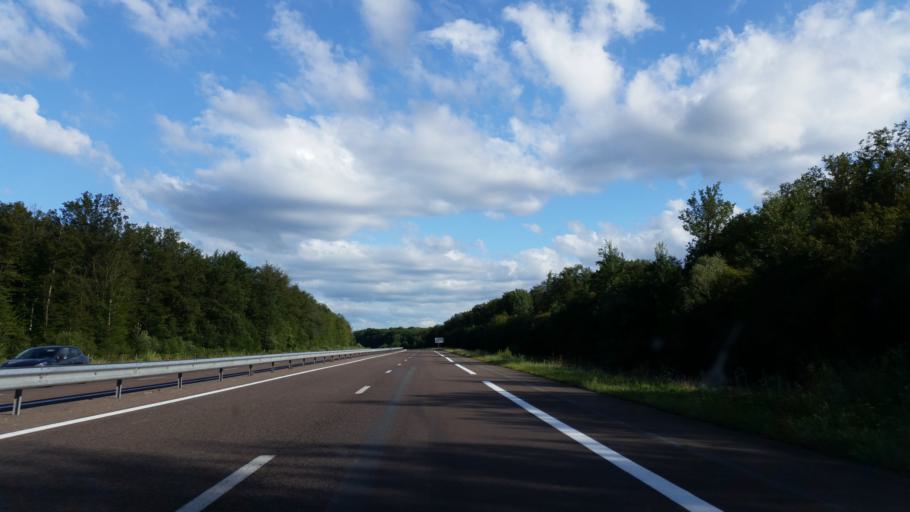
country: FR
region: Franche-Comte
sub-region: Departement de la Haute-Saone
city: Magny-Vernois
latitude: 47.7069
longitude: 6.4581
